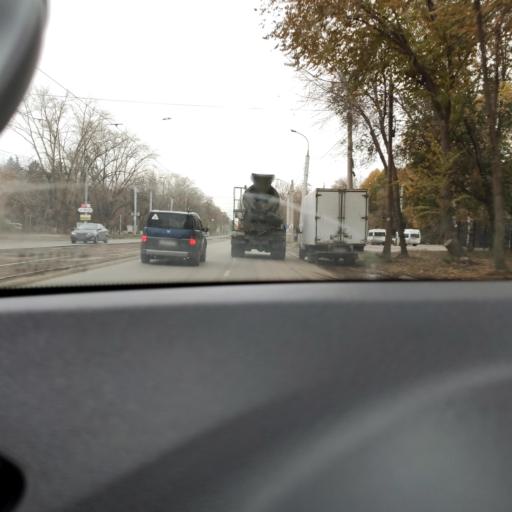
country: RU
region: Samara
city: Smyshlyayevka
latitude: 53.1949
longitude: 50.2915
